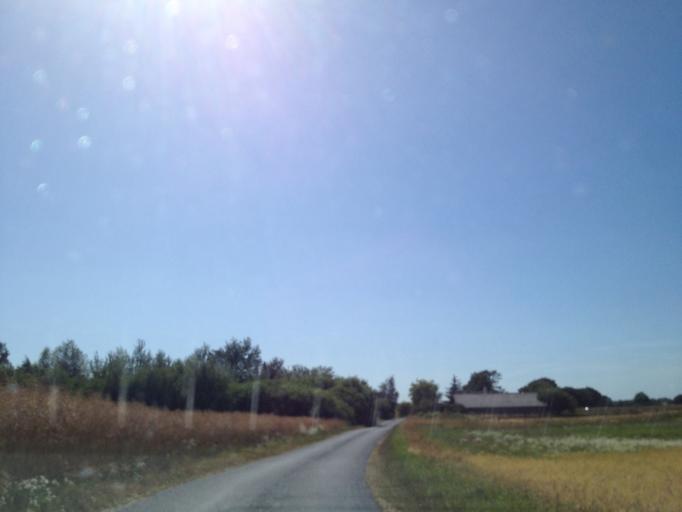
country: DK
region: Capital Region
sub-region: Fredensborg Kommune
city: Fredensborg
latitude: 56.0126
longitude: 12.4649
